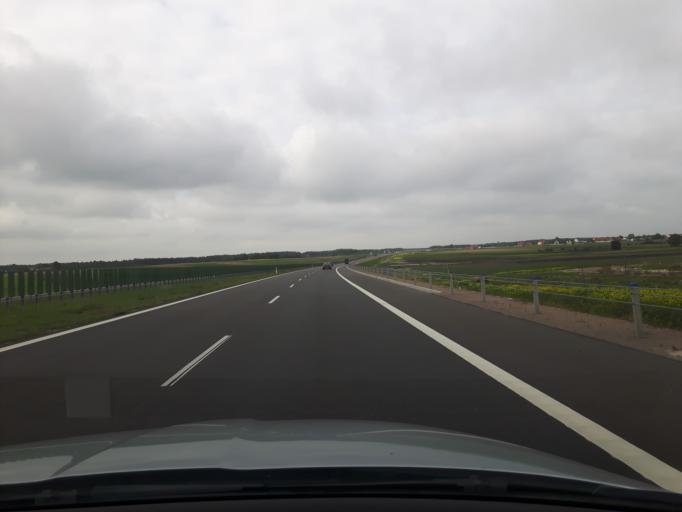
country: PL
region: Swietokrzyskie
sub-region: Powiat jedrzejowski
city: Sobkow
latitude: 50.6959
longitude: 20.3893
